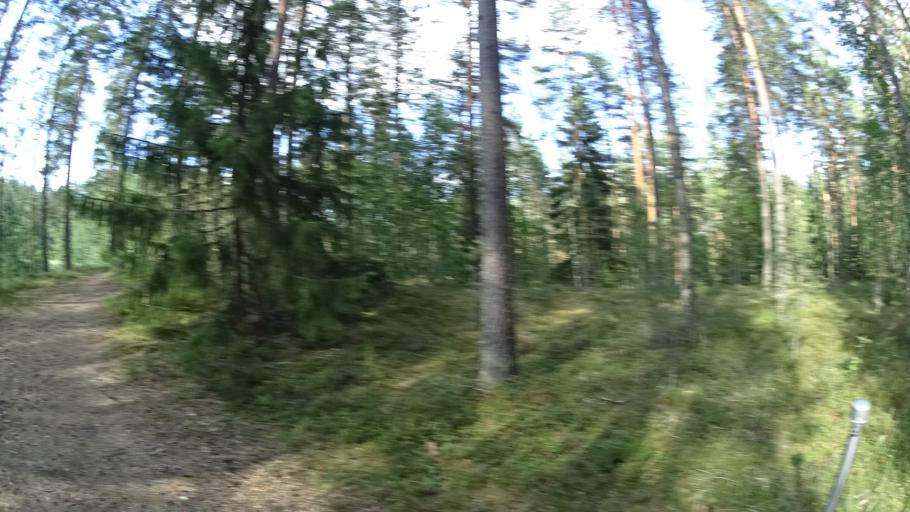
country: FI
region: Uusimaa
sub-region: Helsinki
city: Kaerkoelae
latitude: 60.7355
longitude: 24.0574
